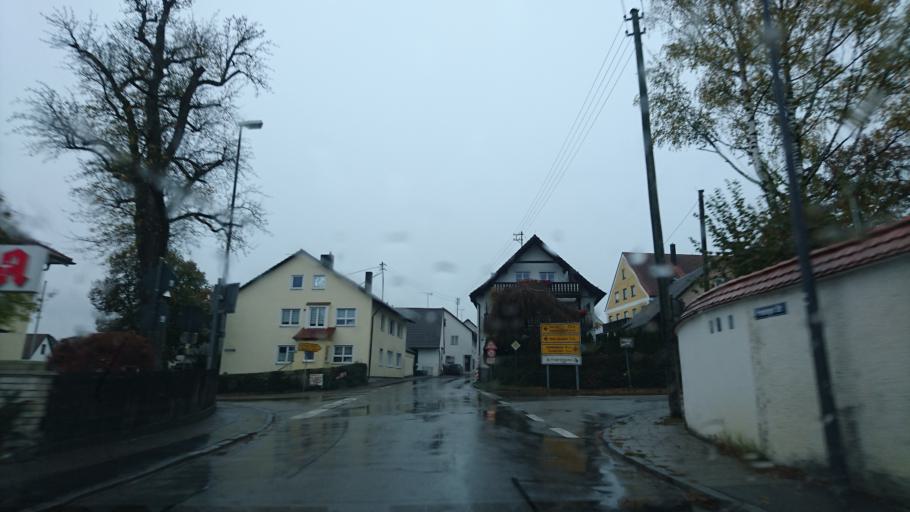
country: DE
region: Bavaria
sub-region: Upper Bavaria
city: Hilgertshausen-Tandern
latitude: 48.4296
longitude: 11.3552
